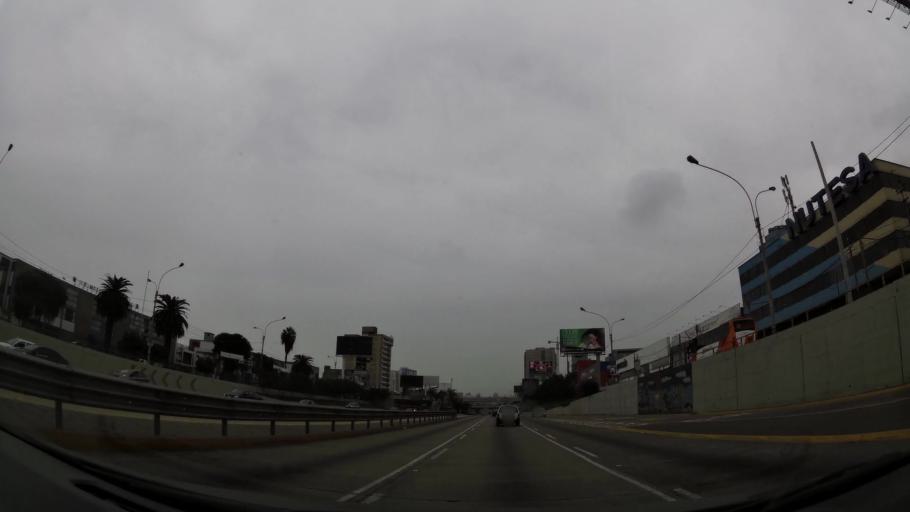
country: PE
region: Lima
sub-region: Lima
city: San Luis
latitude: -12.0847
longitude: -77.0255
